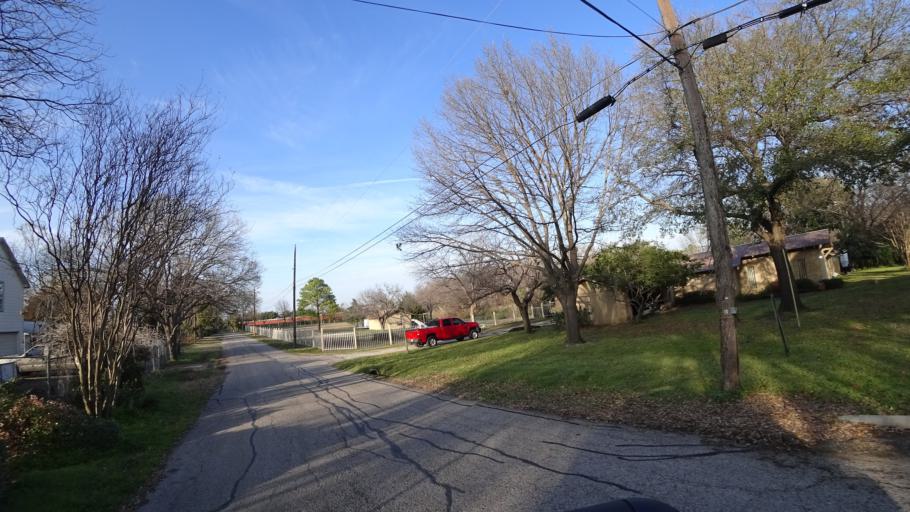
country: US
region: Texas
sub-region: Denton County
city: Lewisville
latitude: 33.0504
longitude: -96.9986
